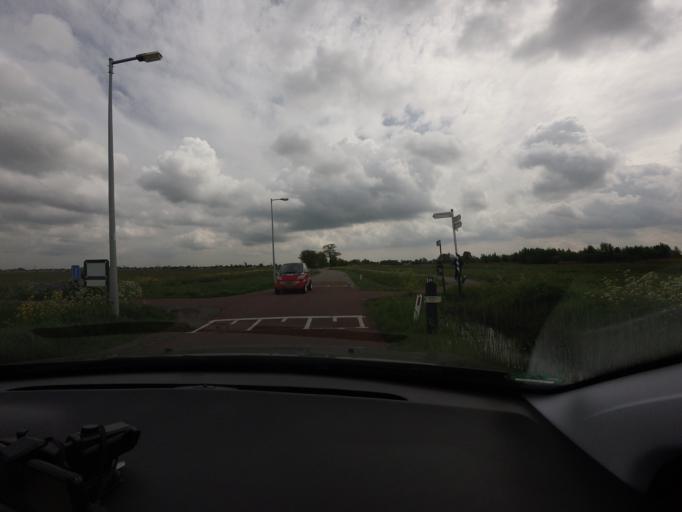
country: NL
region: North Holland
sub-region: Gemeente Landsmeer
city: Landsmeer
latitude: 52.4718
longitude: 4.9047
